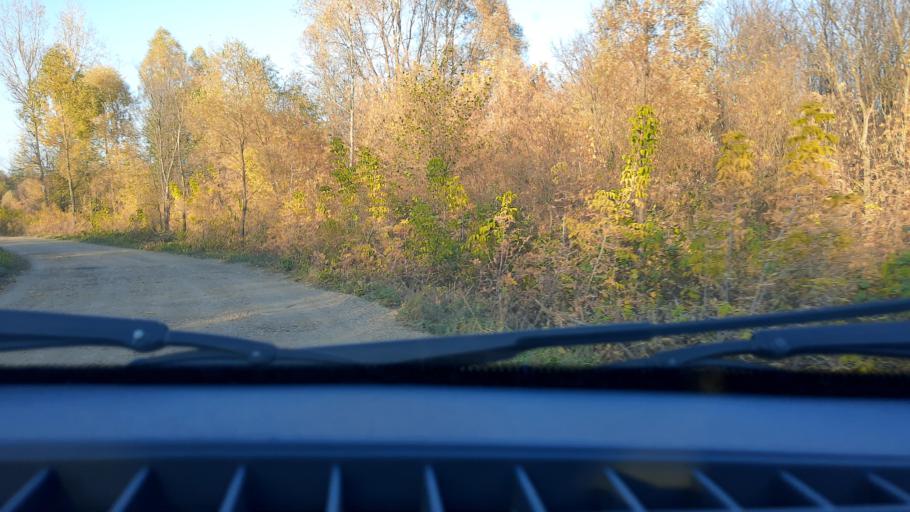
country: RU
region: Bashkortostan
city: Ufa
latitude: 54.7985
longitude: 56.1824
